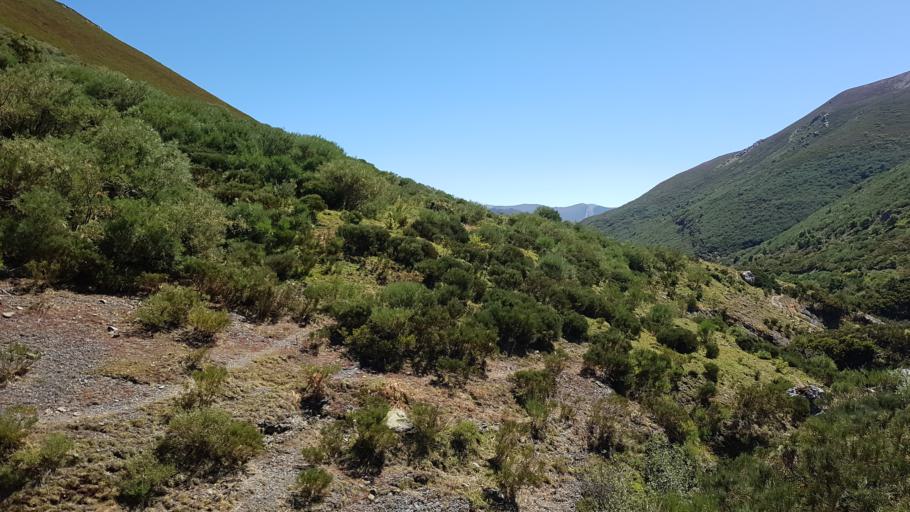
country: ES
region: Asturias
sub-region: Province of Asturias
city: Rio Aller
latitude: 43.0136
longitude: -5.4761
